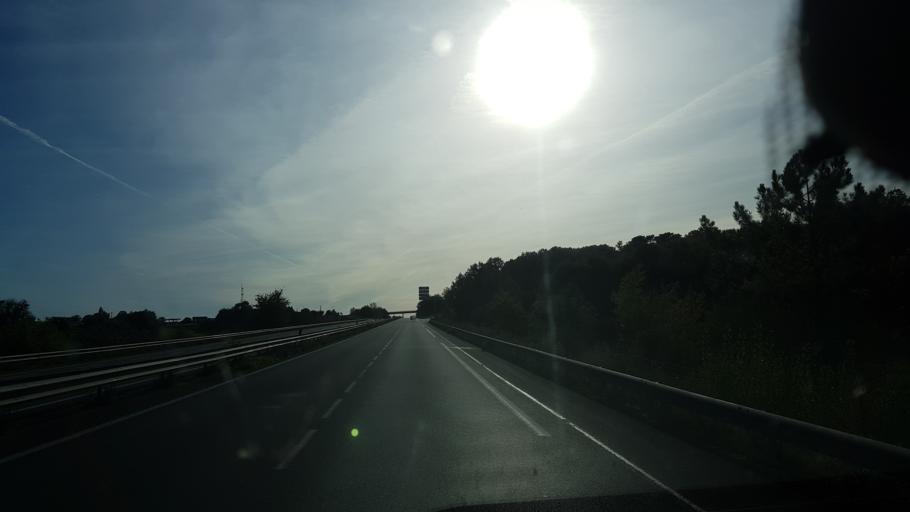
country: FR
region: Poitou-Charentes
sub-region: Departement de la Charente-Maritime
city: Montlieu-la-Garde
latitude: 45.2470
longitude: -0.2674
